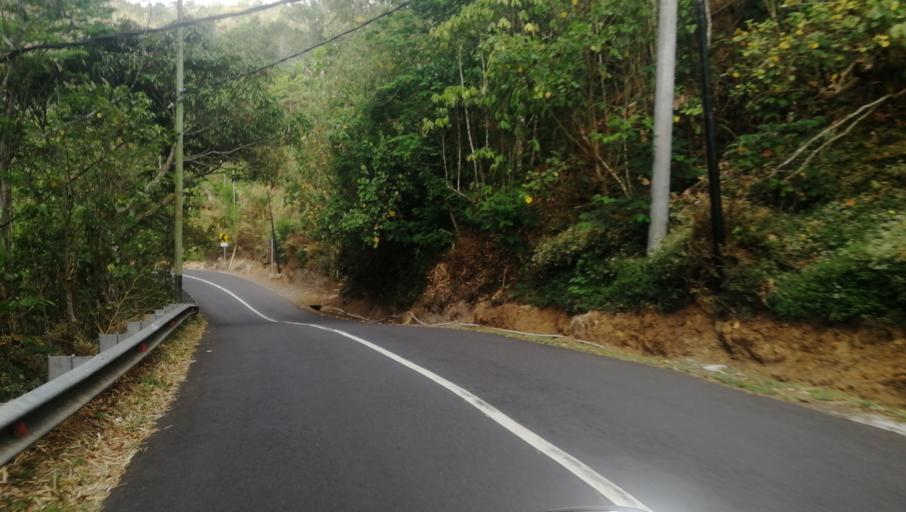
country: ID
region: Bali
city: Munduk
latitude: -8.2553
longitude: 115.0784
